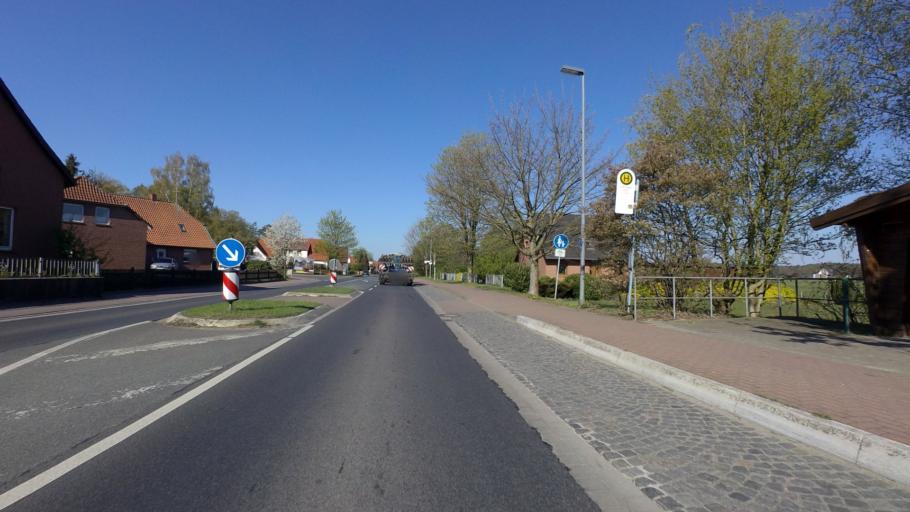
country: DE
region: Lower Saxony
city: Steimbke
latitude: 52.6557
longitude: 9.3963
